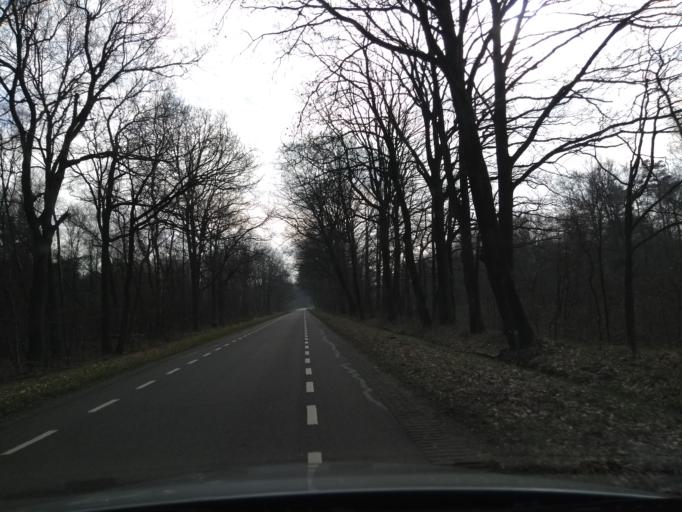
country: NL
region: Overijssel
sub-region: Gemeente Haaksbergen
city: Haaksbergen
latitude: 52.1219
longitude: 6.7489
